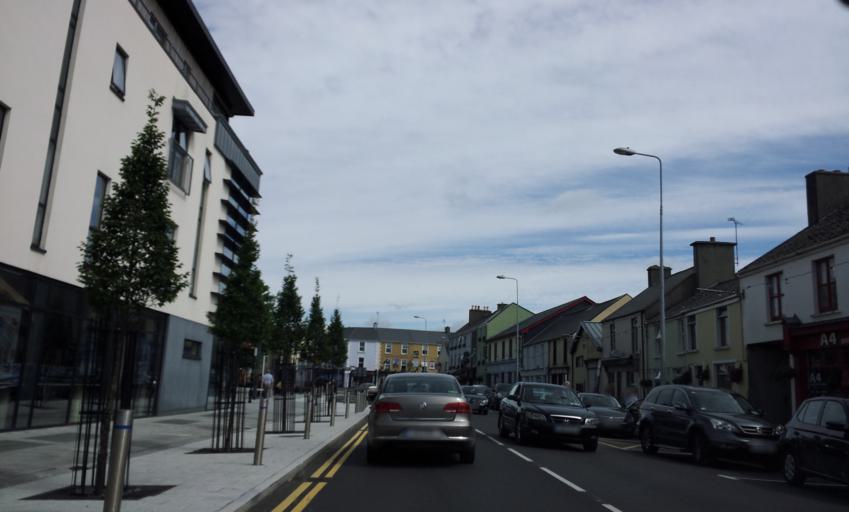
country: IE
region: Munster
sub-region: Ciarrai
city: Killorglin
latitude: 52.1066
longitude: -9.7895
